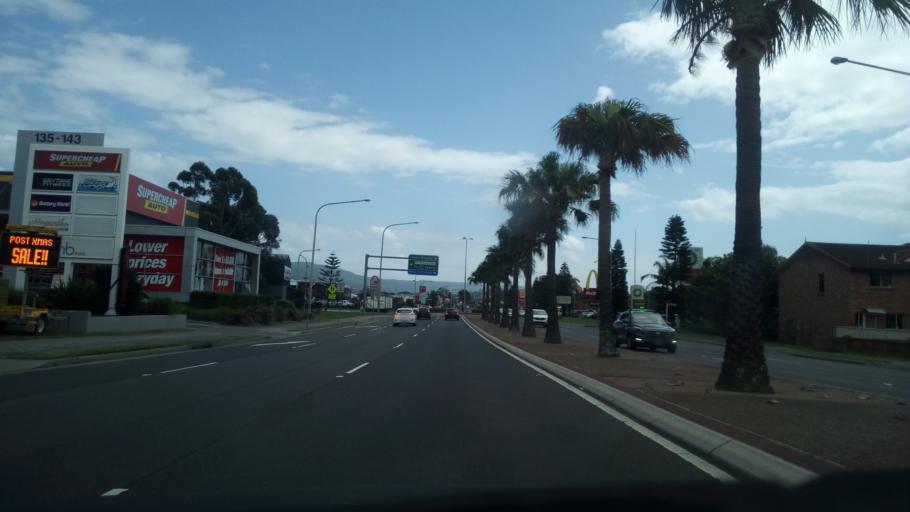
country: AU
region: New South Wales
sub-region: Wollongong
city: Fairy Meadow
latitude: -34.4043
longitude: 150.8909
